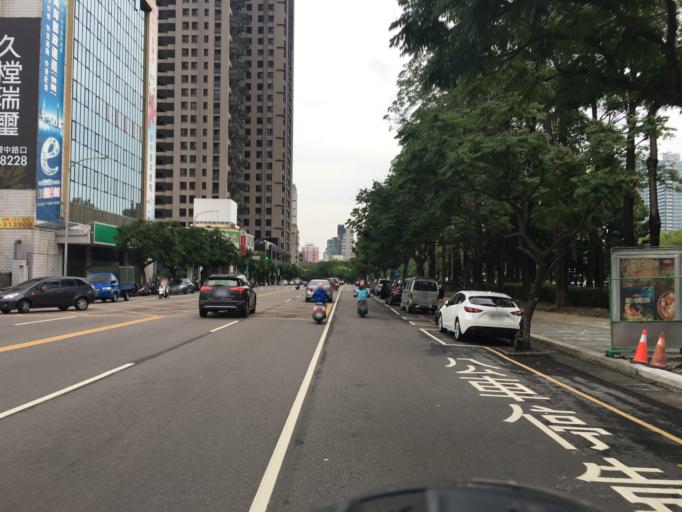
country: TW
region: Taiwan
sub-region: Taichung City
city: Taichung
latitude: 24.1453
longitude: 120.6652
